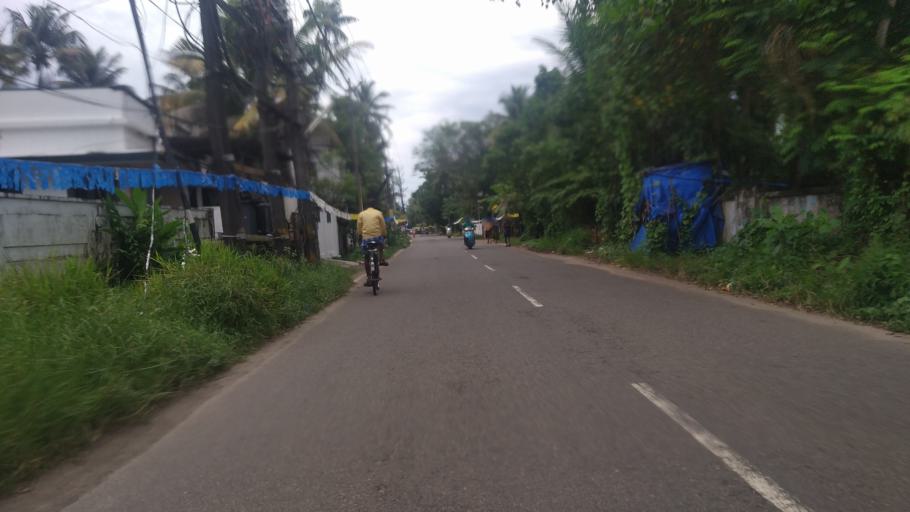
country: IN
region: Kerala
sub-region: Ernakulam
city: Cochin
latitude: 9.8981
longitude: 76.2579
